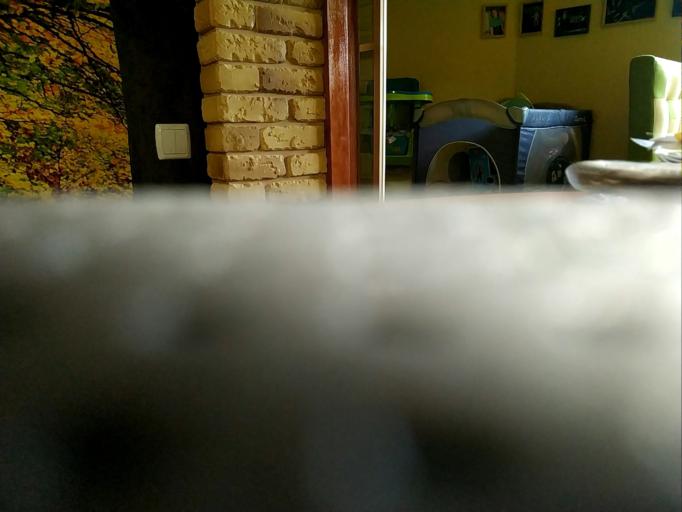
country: RU
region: Kaluga
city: Seredeyskiy
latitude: 53.8961
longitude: 35.3569
